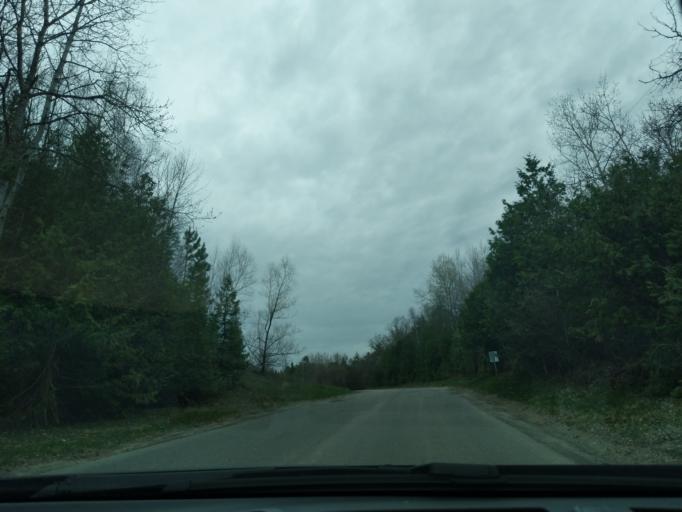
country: CA
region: Ontario
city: Orangeville
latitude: 44.0180
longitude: -79.9683
